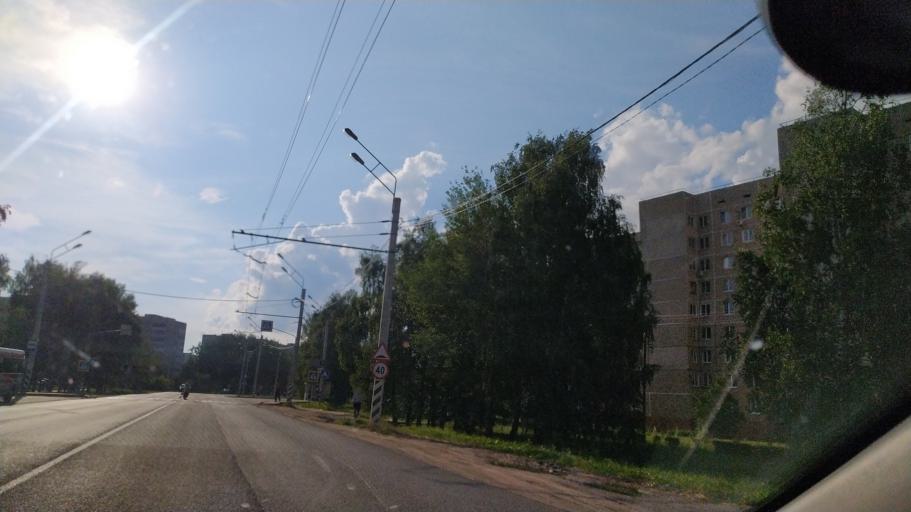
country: RU
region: Chuvashia
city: Novocheboksarsk
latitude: 56.1103
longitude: 47.4483
